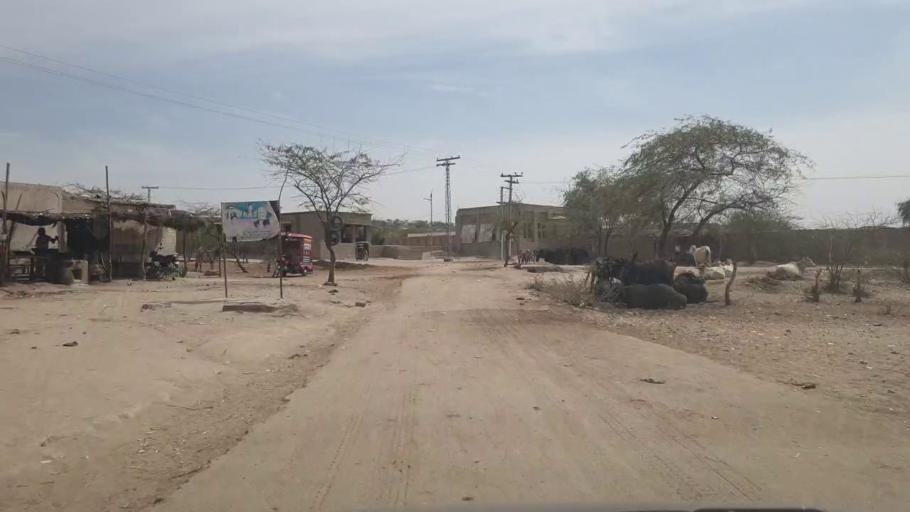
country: PK
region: Sindh
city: Umarkot
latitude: 25.2216
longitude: 69.7146
